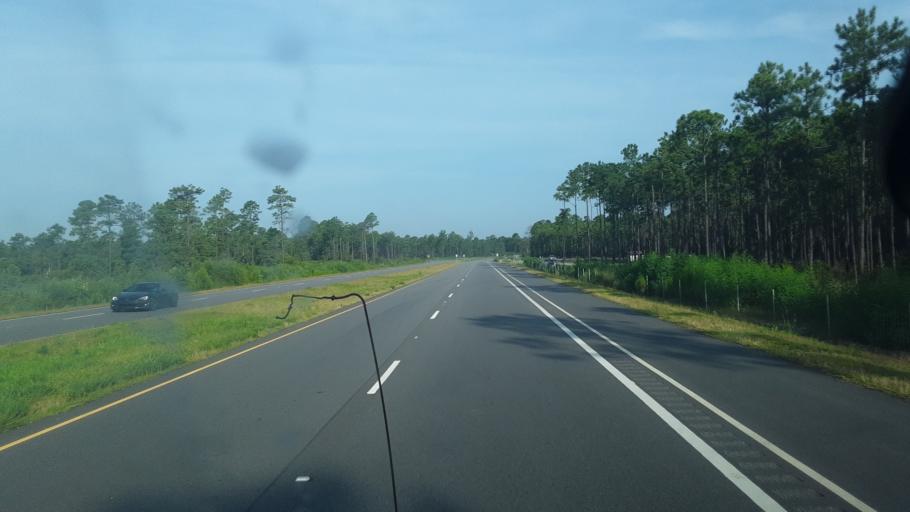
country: US
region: South Carolina
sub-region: Horry County
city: Forestbrook
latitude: 33.8047
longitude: -78.8894
